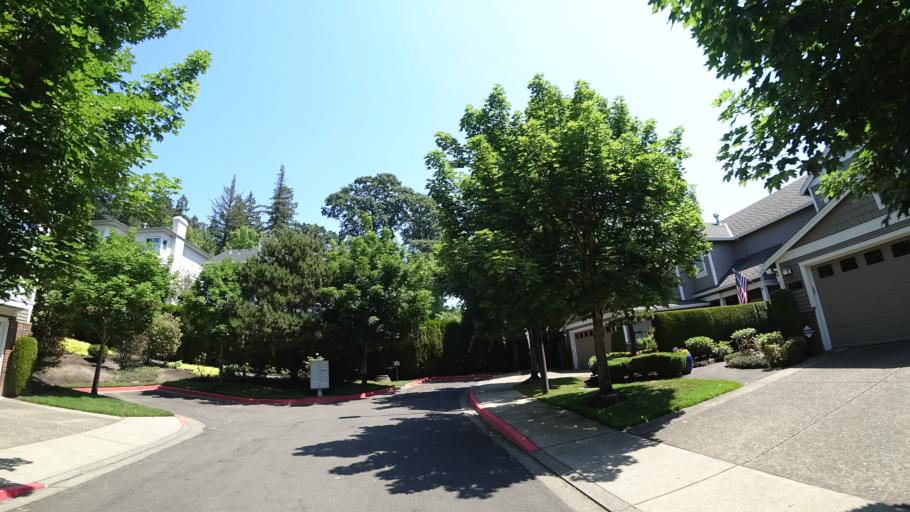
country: US
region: Oregon
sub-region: Washington County
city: Durham
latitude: 45.4264
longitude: -122.7248
